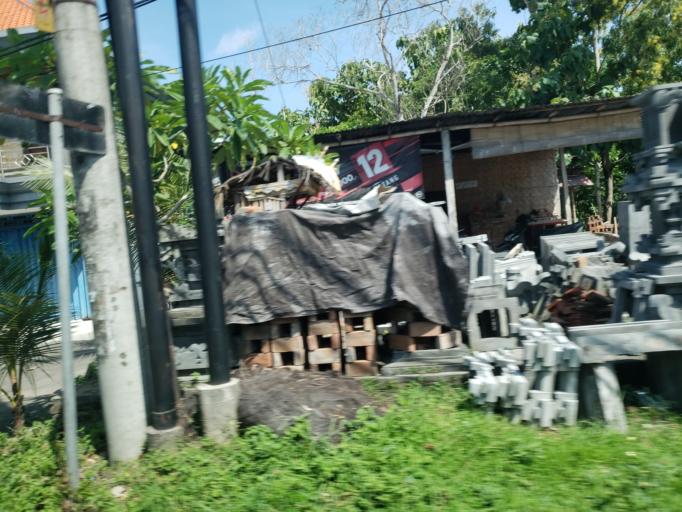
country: ID
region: Bali
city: Kangin
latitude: -8.8253
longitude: 115.1410
